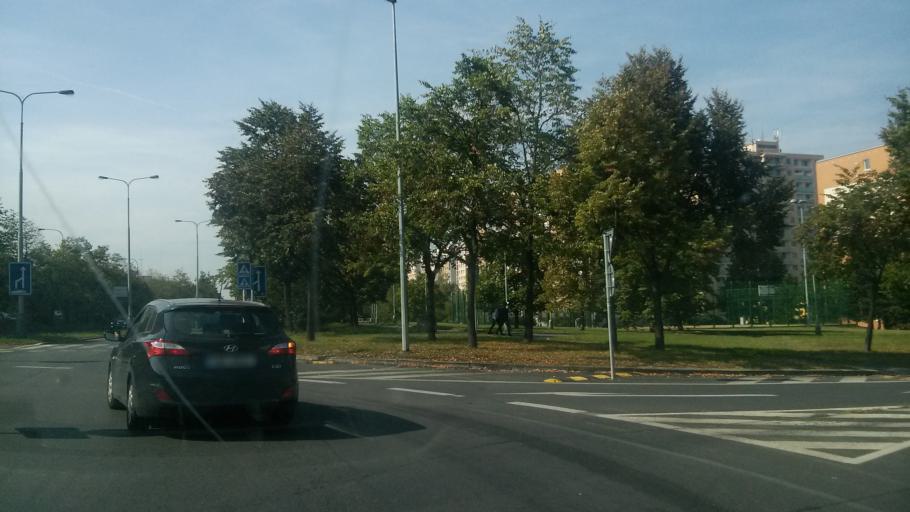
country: CZ
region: Central Bohemia
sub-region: Okres Praha-Zapad
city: Pruhonice
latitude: 50.0326
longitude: 14.5227
